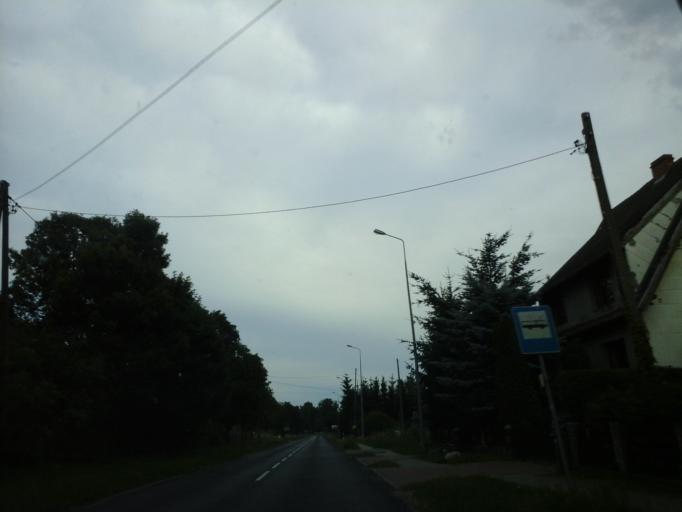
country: PL
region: West Pomeranian Voivodeship
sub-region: Powiat goleniowski
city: Nowogard
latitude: 53.6558
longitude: 15.1324
